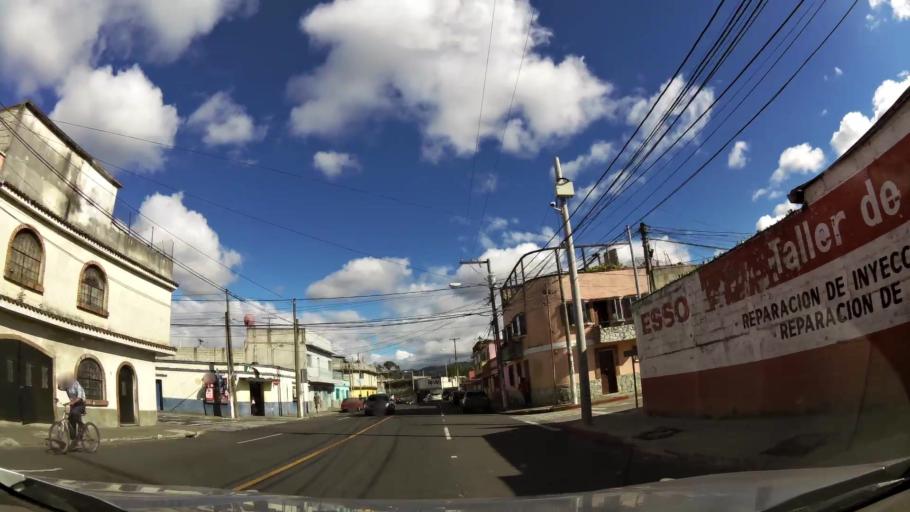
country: GT
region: Guatemala
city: Guatemala City
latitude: 14.6173
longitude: -90.5013
